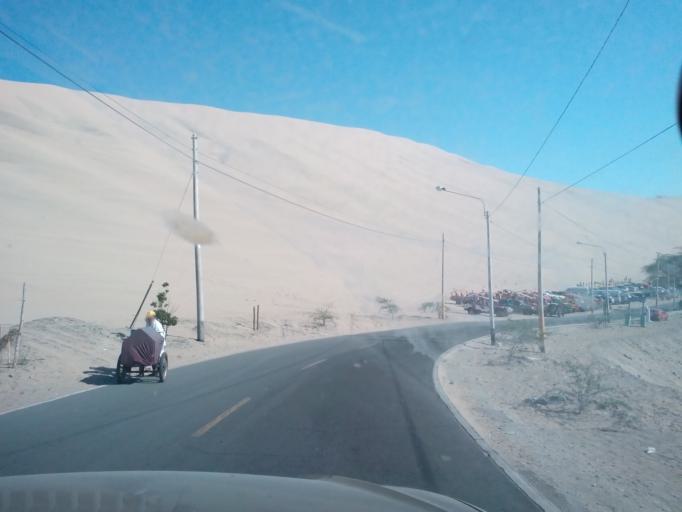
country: PE
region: Ica
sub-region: Provincia de Ica
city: Ica
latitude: -14.0878
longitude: -75.7606
